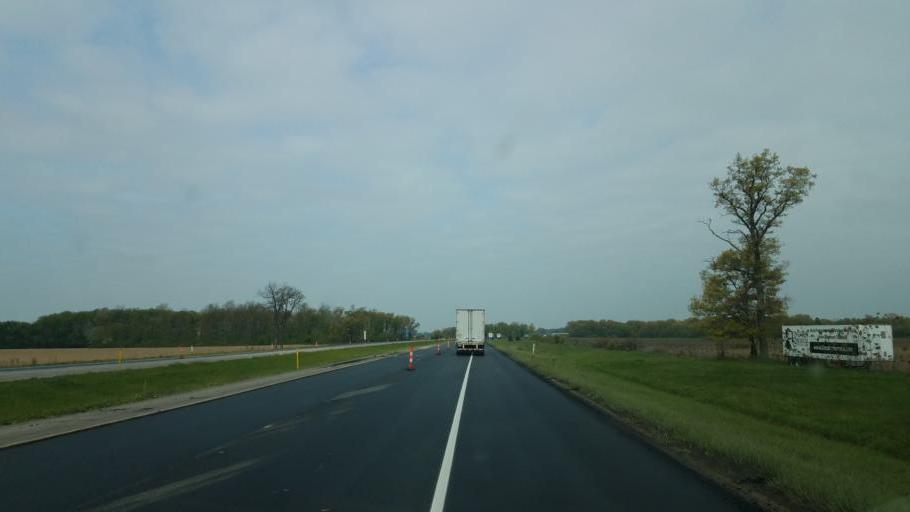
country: US
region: Indiana
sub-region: Saint Joseph County
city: Granger
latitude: 41.7314
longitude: -86.0851
